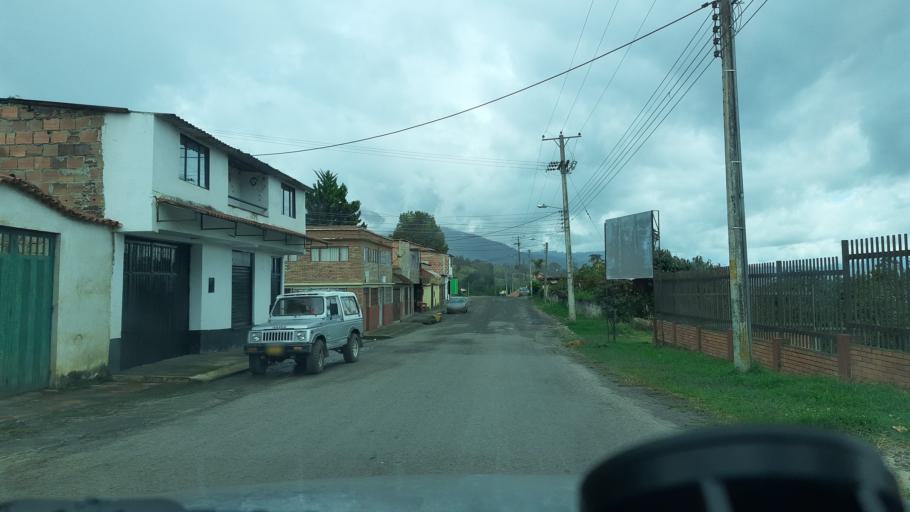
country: CO
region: Boyaca
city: Chinavita
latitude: 5.1674
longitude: -73.3700
